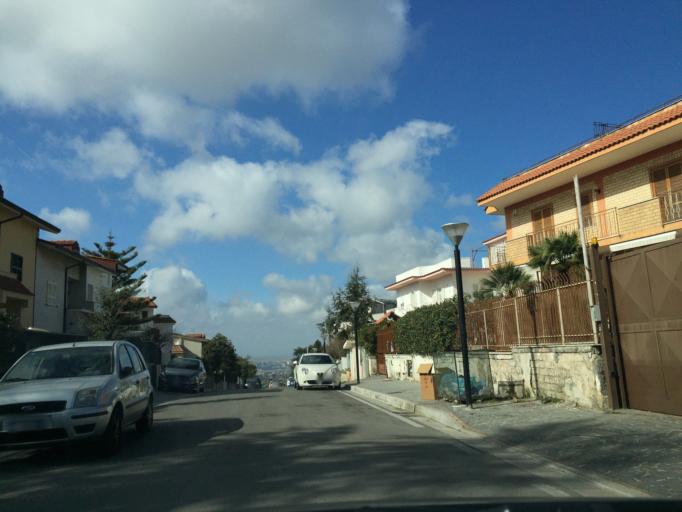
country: IT
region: Campania
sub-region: Provincia di Napoli
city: Pollena Trocchia
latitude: 40.8502
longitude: 14.3829
